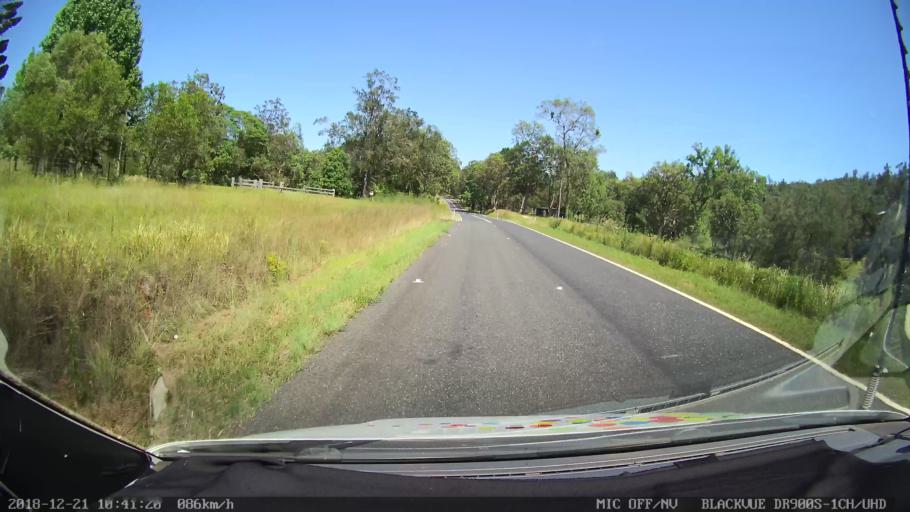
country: AU
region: New South Wales
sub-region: Clarence Valley
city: Gordon
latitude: -29.5919
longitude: 152.5760
